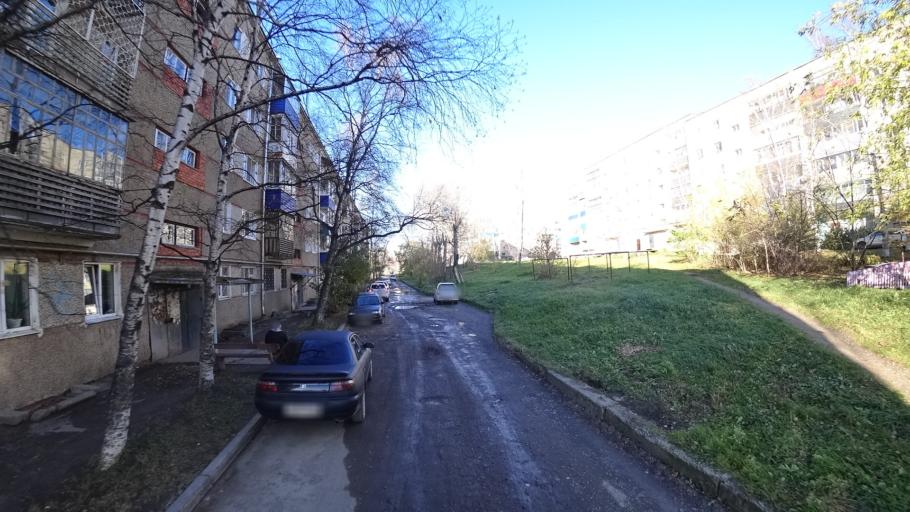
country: RU
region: Khabarovsk Krai
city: Amursk
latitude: 50.2306
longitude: 136.9112
